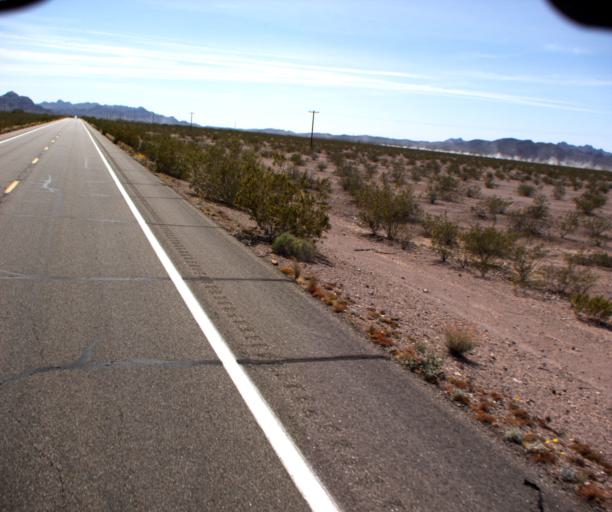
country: US
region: Arizona
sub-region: La Paz County
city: Quartzsite
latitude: 33.3492
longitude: -114.2171
